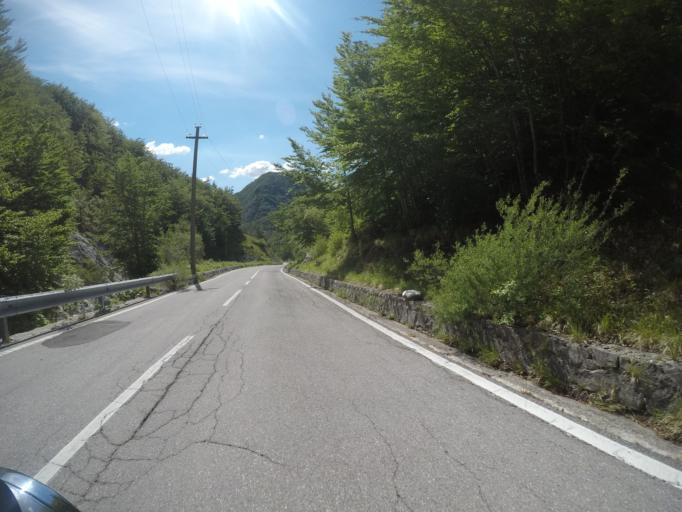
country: IT
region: Tuscany
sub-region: Provincia di Lucca
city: Seravezza
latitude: 44.0611
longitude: 10.2363
